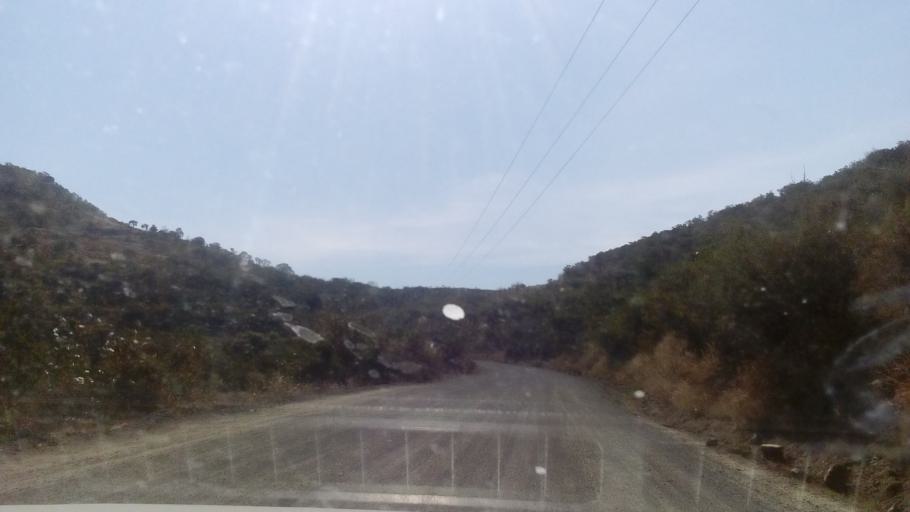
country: MX
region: Guanajuato
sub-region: Leon
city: Medina
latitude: 21.1513
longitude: -101.5972
